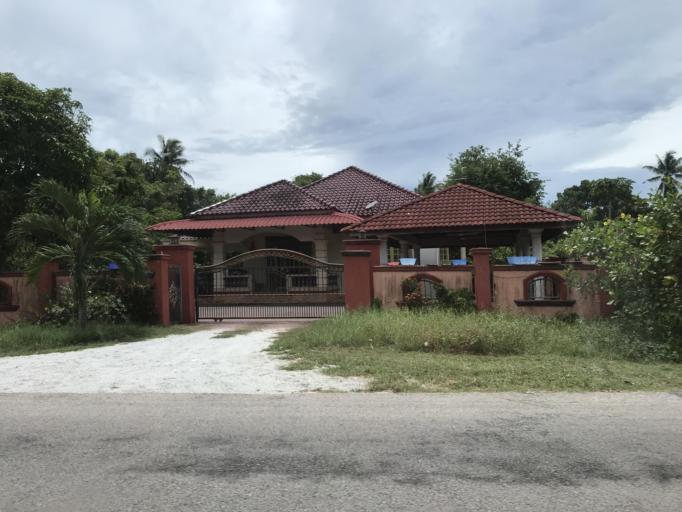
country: MY
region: Kelantan
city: Tumpat
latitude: 6.1766
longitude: 102.1919
